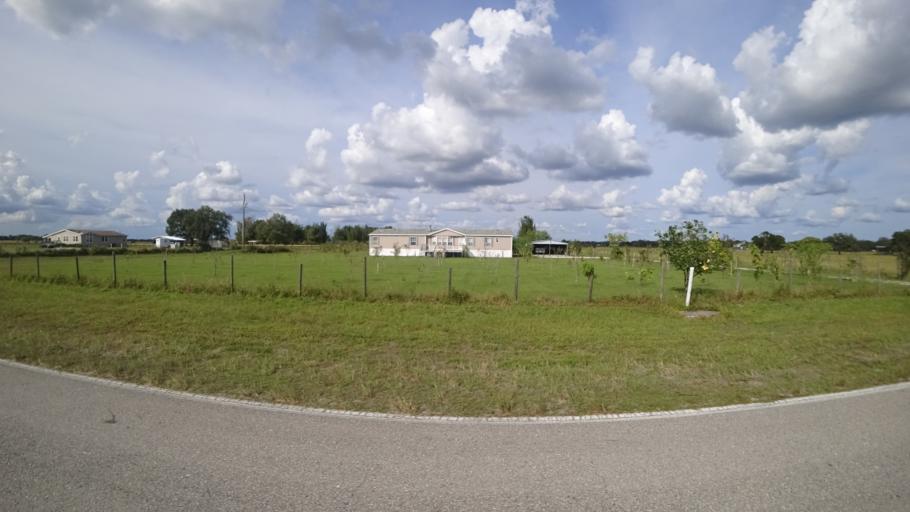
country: US
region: Florida
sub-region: Sarasota County
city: Lake Sarasota
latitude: 27.3391
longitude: -82.1792
